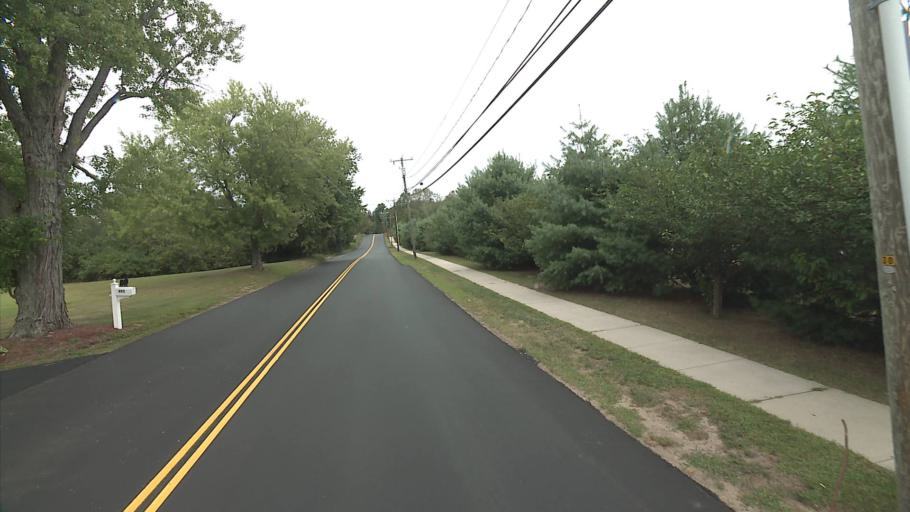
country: US
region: Connecticut
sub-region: New London County
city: Colchester
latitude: 41.5928
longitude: -72.3391
